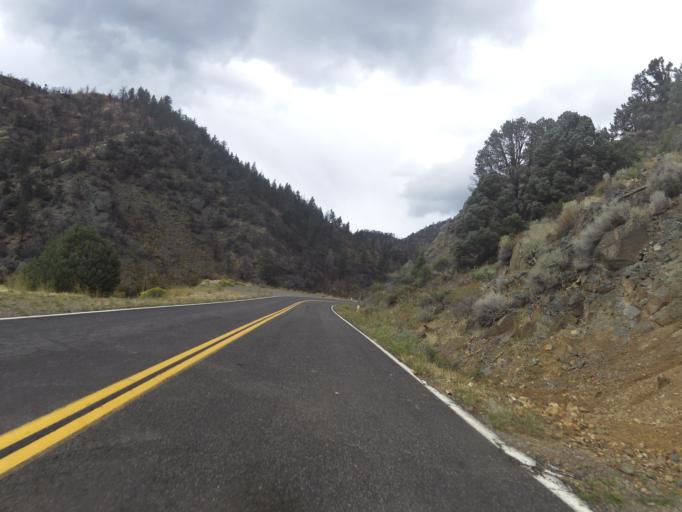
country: US
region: Nevada
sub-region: Douglas County
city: Gardnerville Ranchos
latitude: 38.6623
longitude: -119.6865
